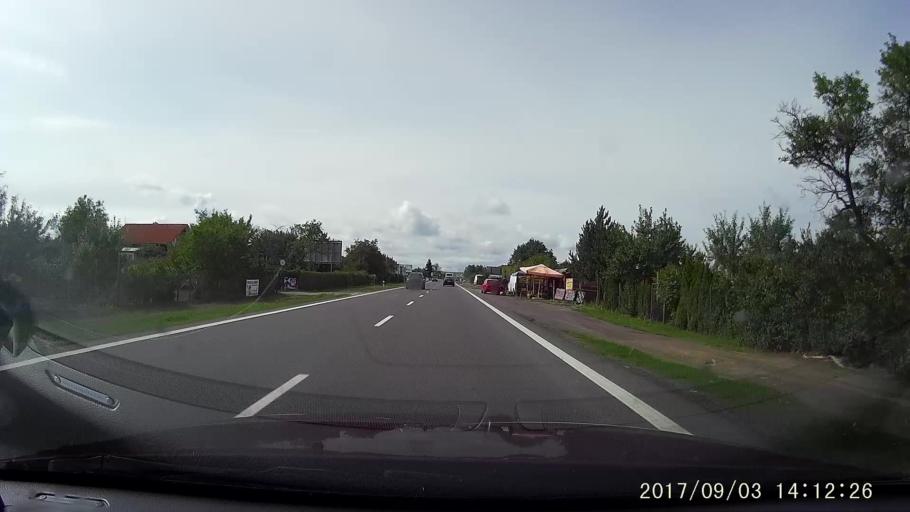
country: CZ
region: South Moravian
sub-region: Okres Znojmo
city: Znojmo
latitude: 48.8712
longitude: 16.0278
